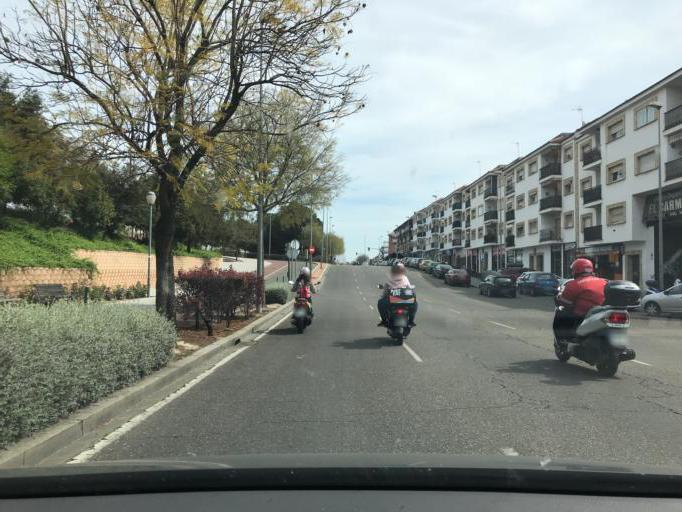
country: ES
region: Andalusia
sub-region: Province of Cordoba
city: Cordoba
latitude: 37.8949
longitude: -4.7748
